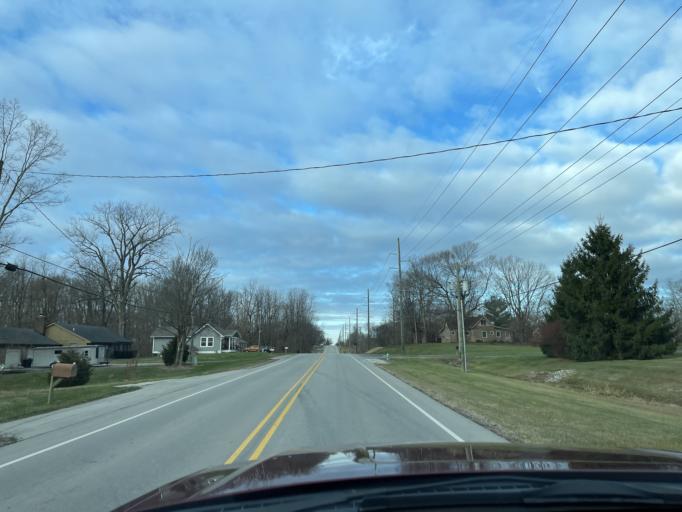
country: US
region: Indiana
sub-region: Hendricks County
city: Avon
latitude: 39.7621
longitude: -86.4488
